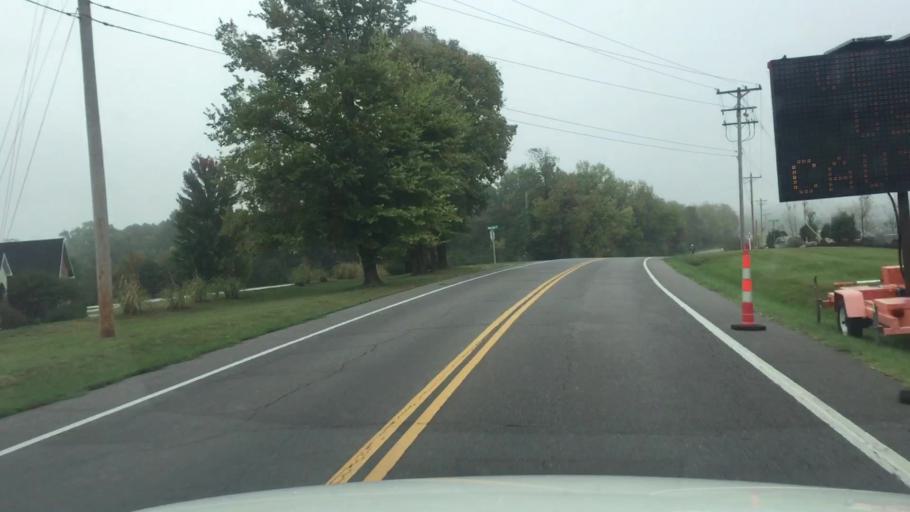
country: US
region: Missouri
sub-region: Boone County
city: Columbia
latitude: 38.8700
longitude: -92.3942
